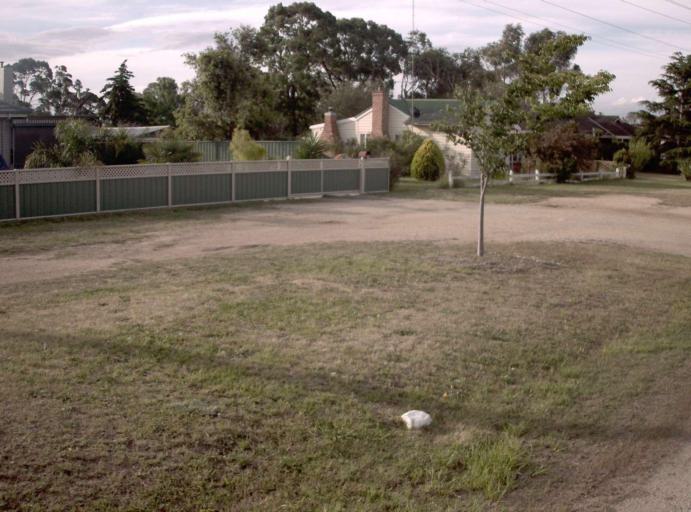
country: AU
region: Victoria
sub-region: Wellington
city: Sale
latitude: -37.9562
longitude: 146.9870
